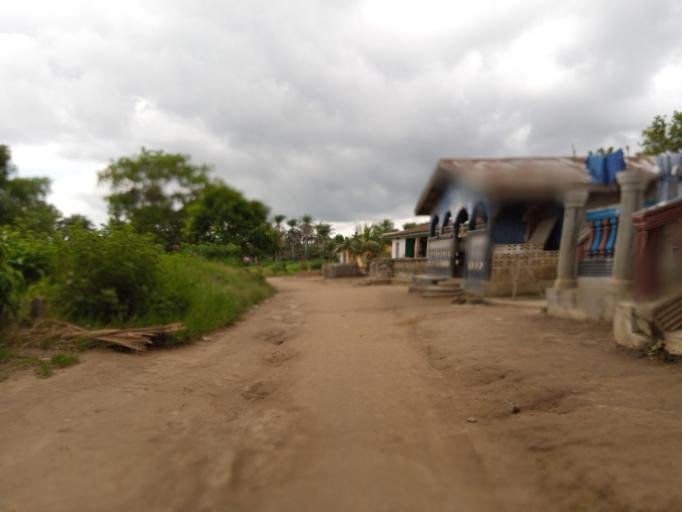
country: SL
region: Northern Province
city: Masoyila
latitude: 8.5768
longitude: -13.1625
